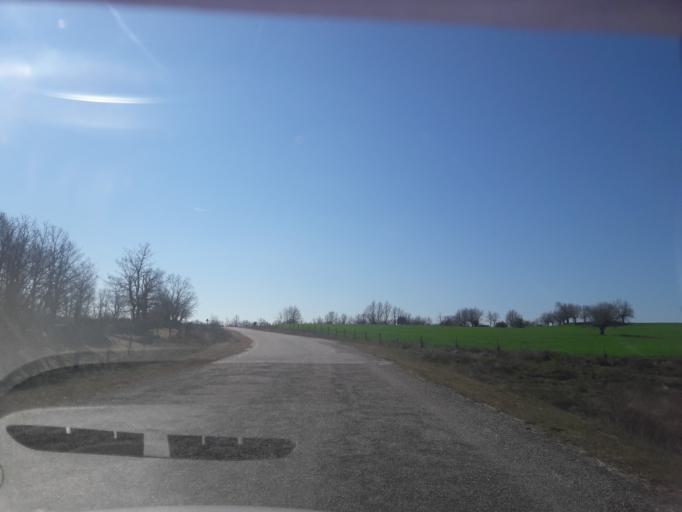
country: ES
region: Castille and Leon
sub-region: Provincia de Salamanca
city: Valsalabroso
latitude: 41.1605
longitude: -6.4956
